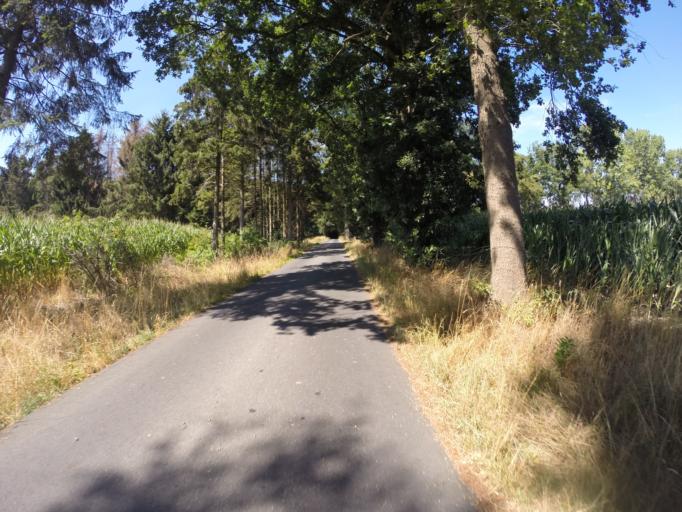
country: BE
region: Flanders
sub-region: Provincie Oost-Vlaanderen
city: Knesselare
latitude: 51.0994
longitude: 3.3937
